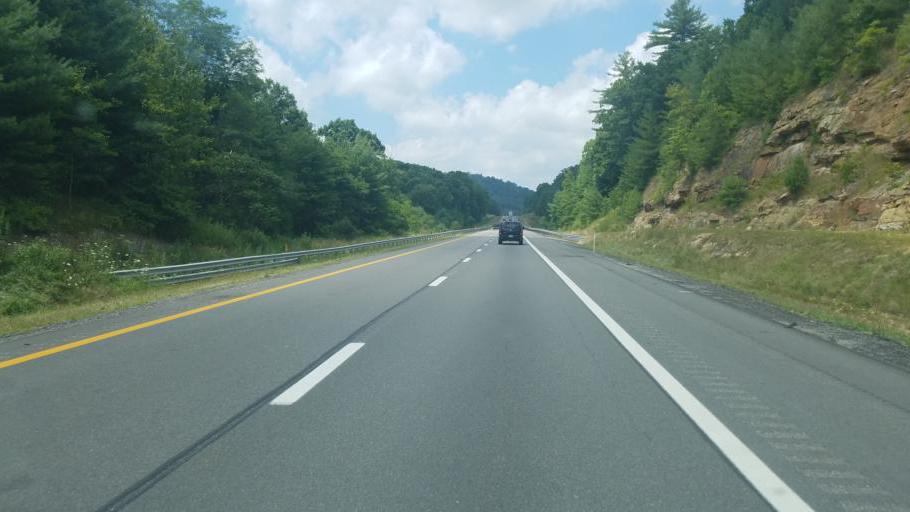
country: US
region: West Virginia
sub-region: Raleigh County
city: Shady Spring
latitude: 37.7012
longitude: -81.1405
